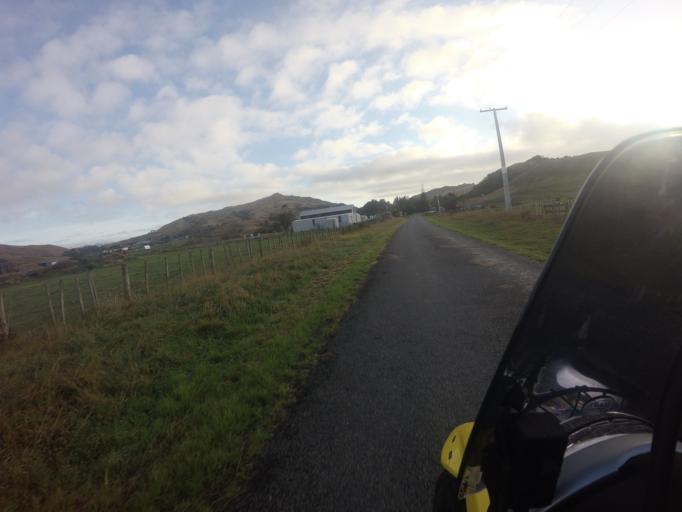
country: NZ
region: Gisborne
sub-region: Gisborne District
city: Gisborne
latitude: -38.6702
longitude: 178.0825
